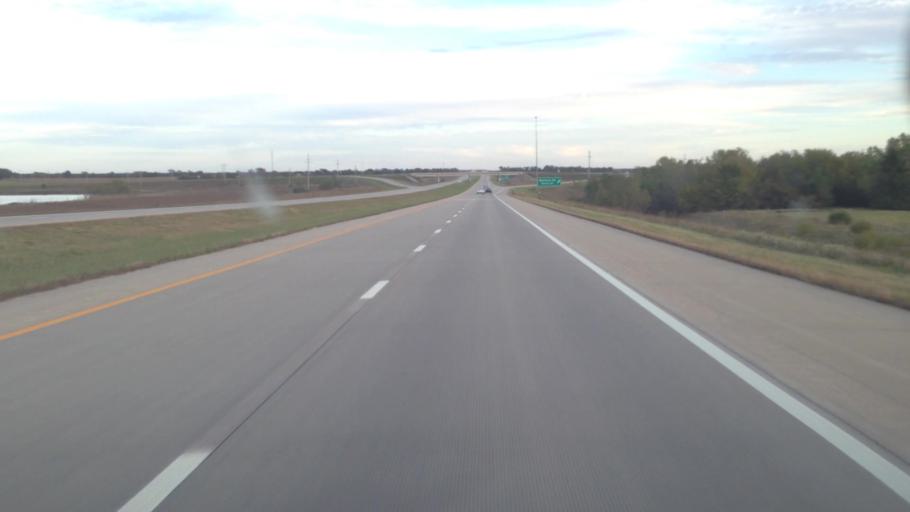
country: US
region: Kansas
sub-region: Franklin County
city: Ottawa
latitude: 38.6702
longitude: -95.2565
